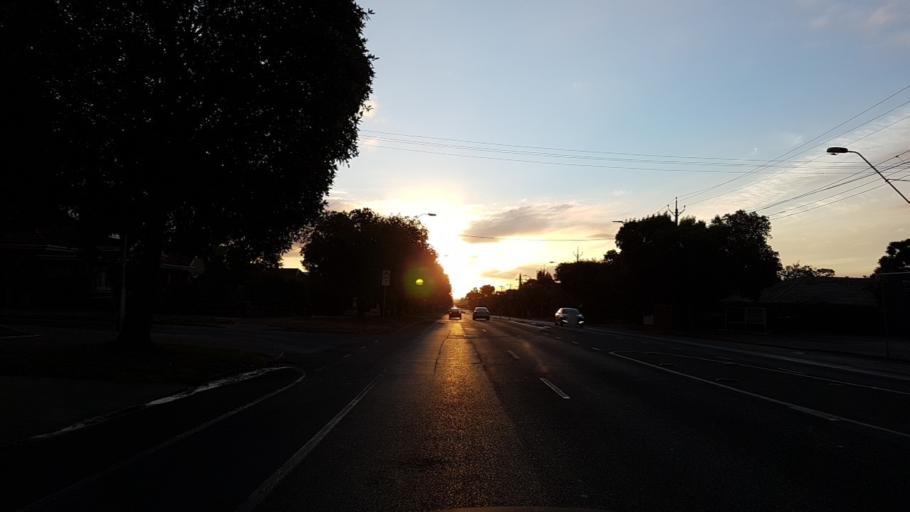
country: AU
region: South Australia
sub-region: Burnside
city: Tusmore
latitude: -34.9389
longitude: 138.6504
